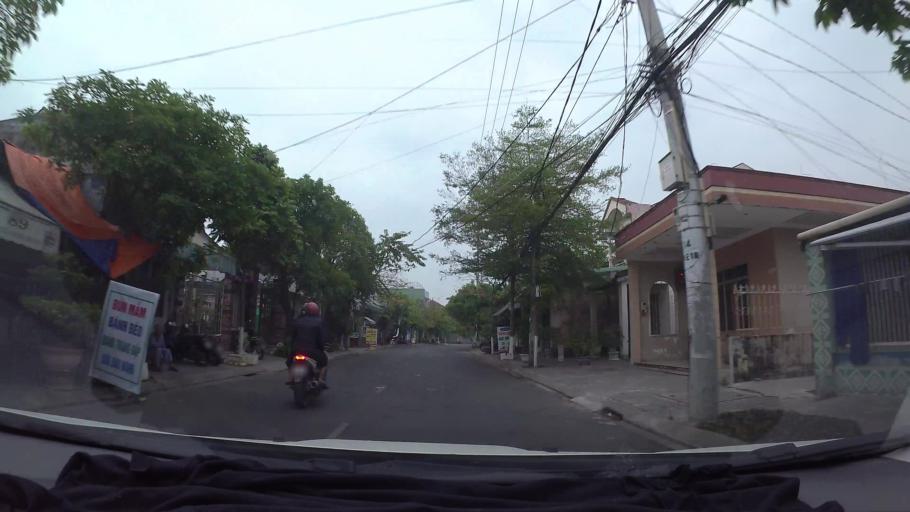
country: VN
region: Da Nang
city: Thanh Khe
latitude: 16.0549
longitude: 108.1751
